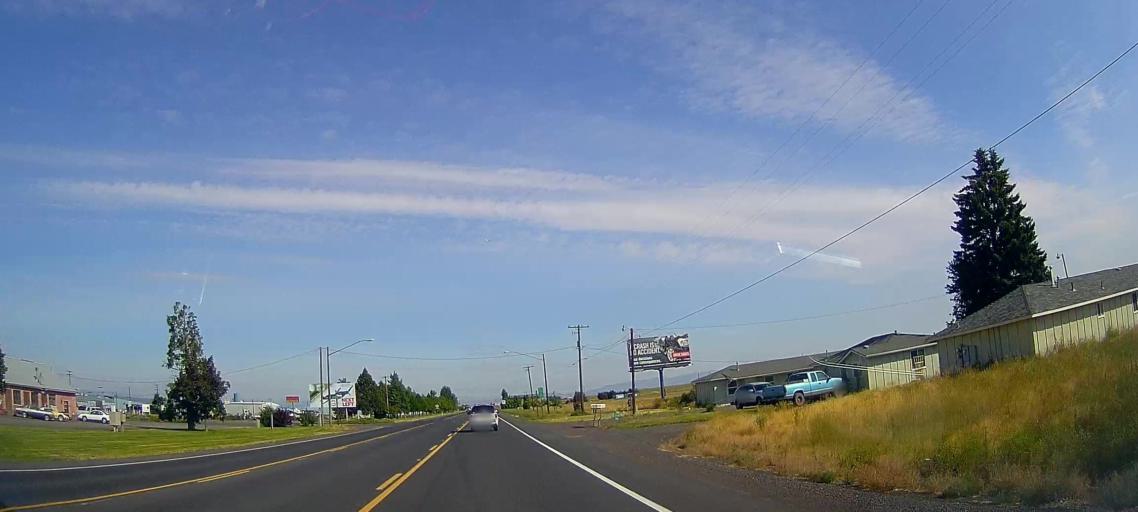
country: US
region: Oregon
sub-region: Jefferson County
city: Madras
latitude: 44.6604
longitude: -121.1328
